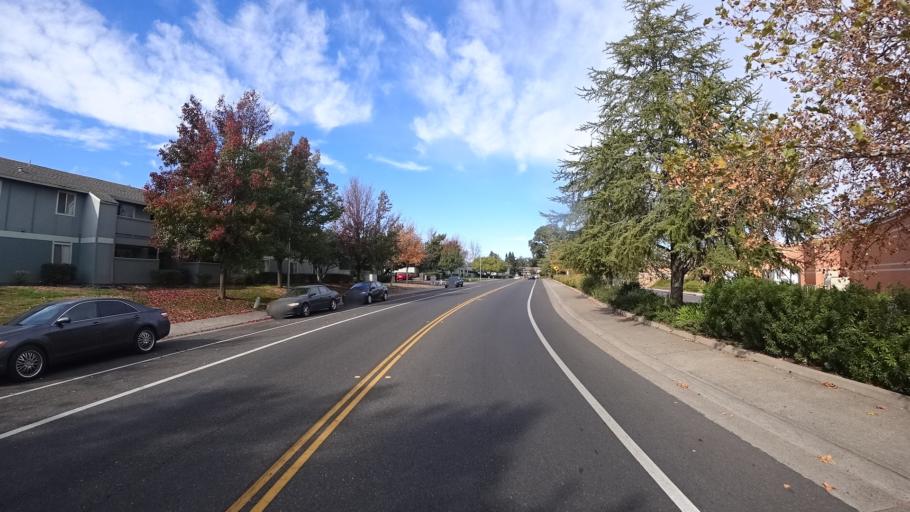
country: US
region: California
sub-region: Sacramento County
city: Fair Oaks
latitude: 38.6719
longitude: -121.2754
